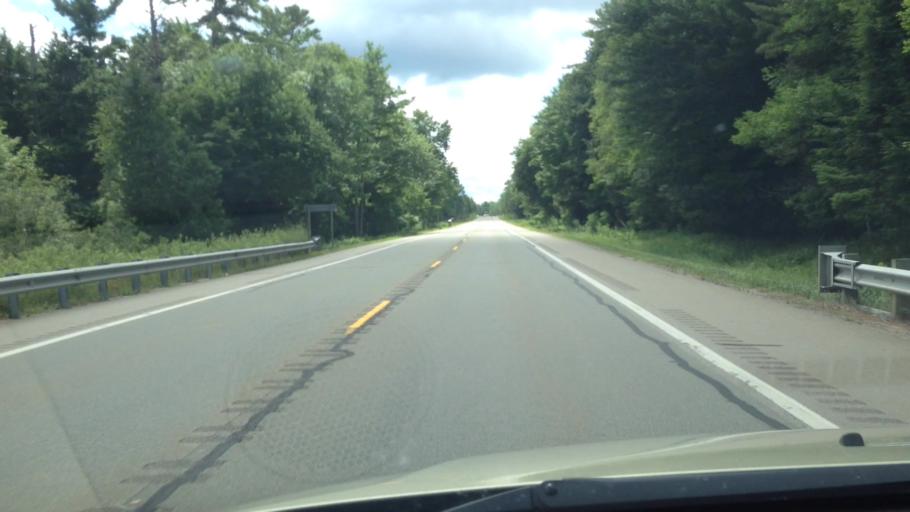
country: US
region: Michigan
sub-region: Menominee County
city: Menominee
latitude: 45.3194
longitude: -87.4316
